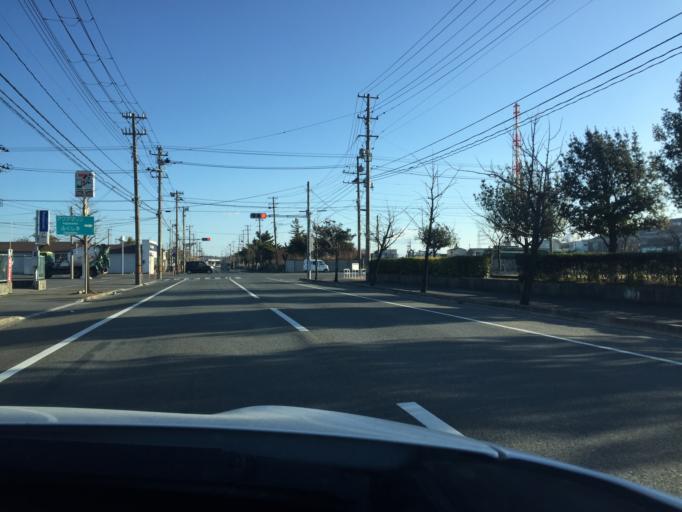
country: JP
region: Fukushima
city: Iwaki
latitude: 36.9425
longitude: 140.8740
